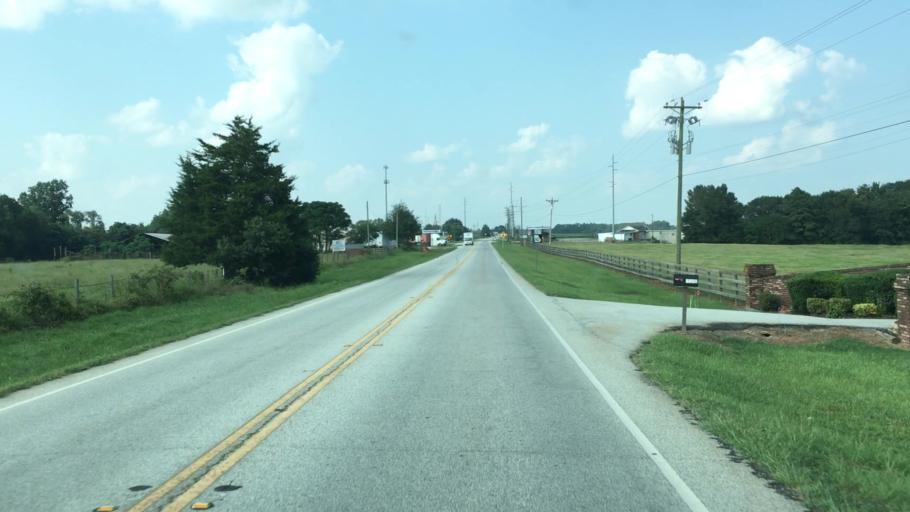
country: US
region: Georgia
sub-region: Walton County
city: Social Circle
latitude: 33.5492
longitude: -83.7400
